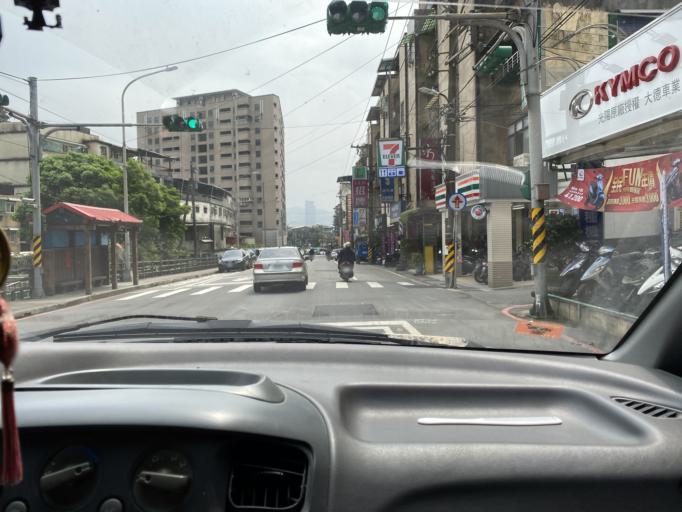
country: TW
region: Taiwan
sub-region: Keelung
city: Keelung
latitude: 25.1478
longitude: 121.7380
